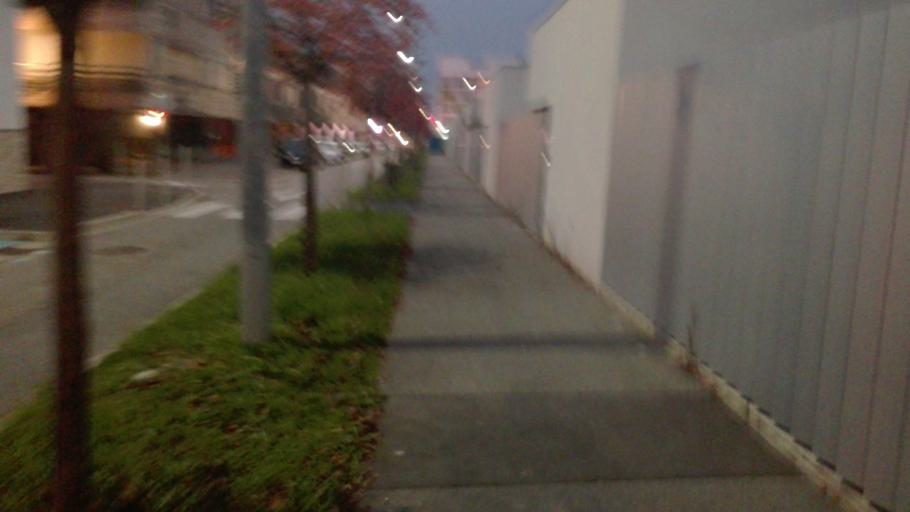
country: FR
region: Midi-Pyrenees
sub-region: Departement de la Haute-Garonne
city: Beauzelle
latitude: 43.6545
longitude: 1.3697
